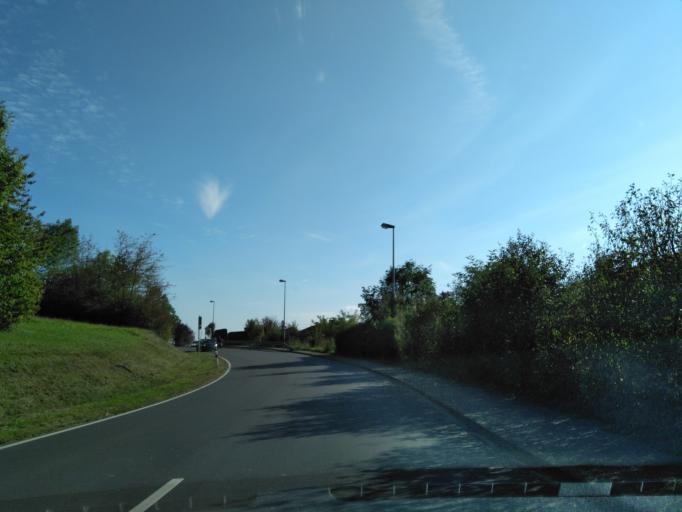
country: DE
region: Baden-Wuerttemberg
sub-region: Regierungsbezirk Stuttgart
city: Freudental
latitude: 48.9691
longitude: 9.0760
